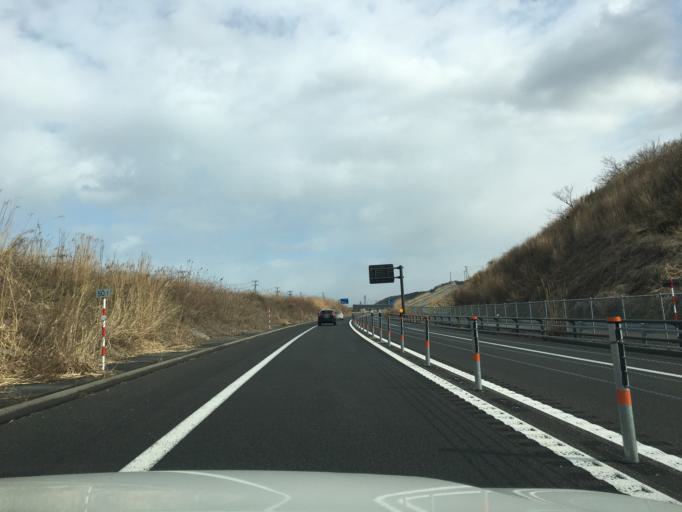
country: JP
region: Yamagata
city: Yuza
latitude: 39.3025
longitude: 139.9776
